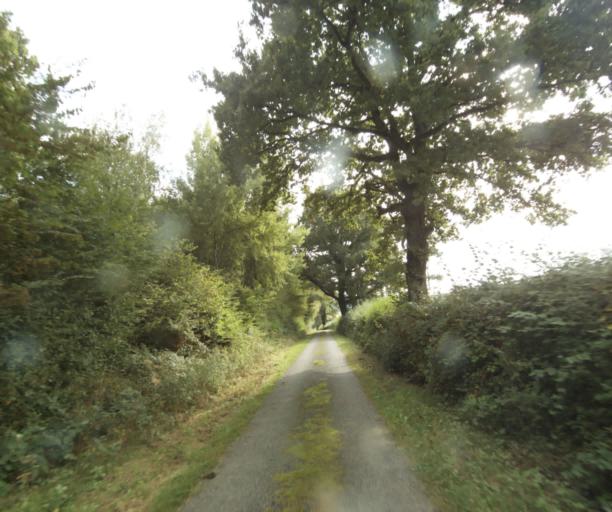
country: FR
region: Bourgogne
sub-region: Departement de Saone-et-Loire
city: Palinges
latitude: 46.5148
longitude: 4.2452
